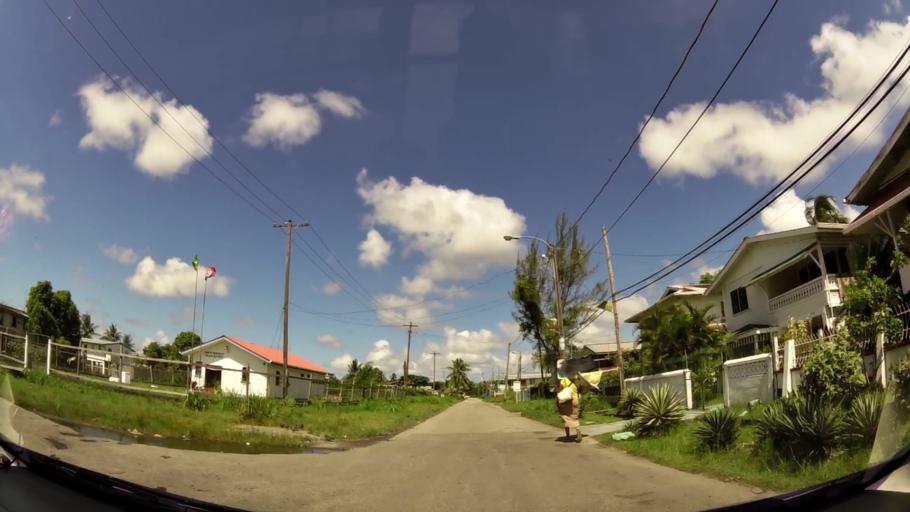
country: GY
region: Demerara-Mahaica
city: Georgetown
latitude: 6.7820
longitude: -58.1242
